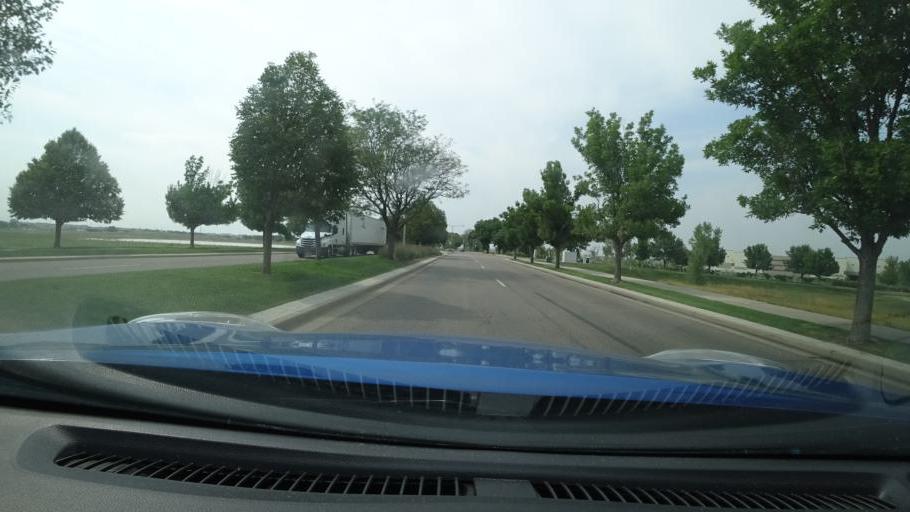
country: US
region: Colorado
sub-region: Adams County
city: Aurora
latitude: 39.7601
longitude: -104.7620
